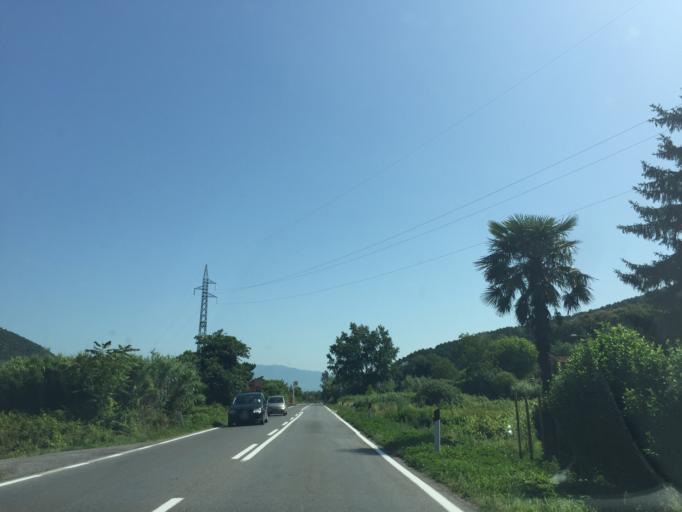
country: IT
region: Tuscany
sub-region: Province of Pisa
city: Asciano
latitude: 43.7848
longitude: 10.4675
